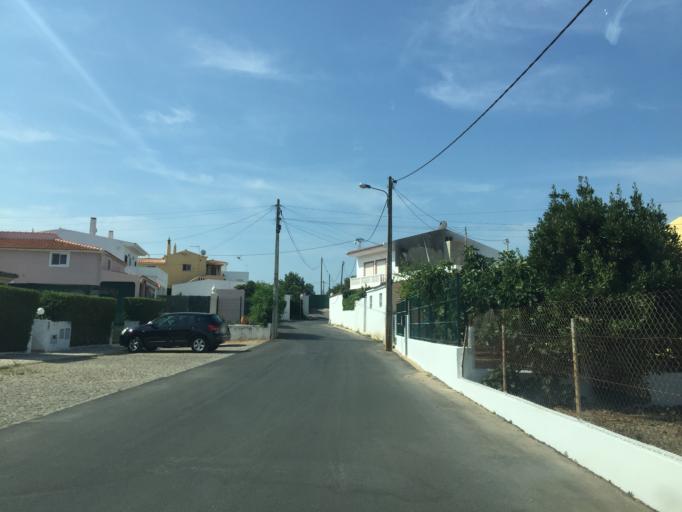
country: PT
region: Faro
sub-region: Loule
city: Almancil
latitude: 37.0920
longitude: -8.0313
